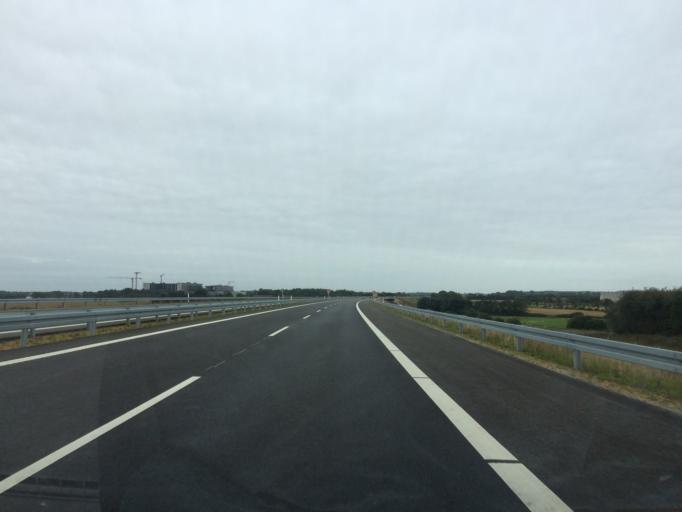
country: DK
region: Central Jutland
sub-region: Herning Kommune
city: Snejbjerg
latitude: 56.1704
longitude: 8.8905
